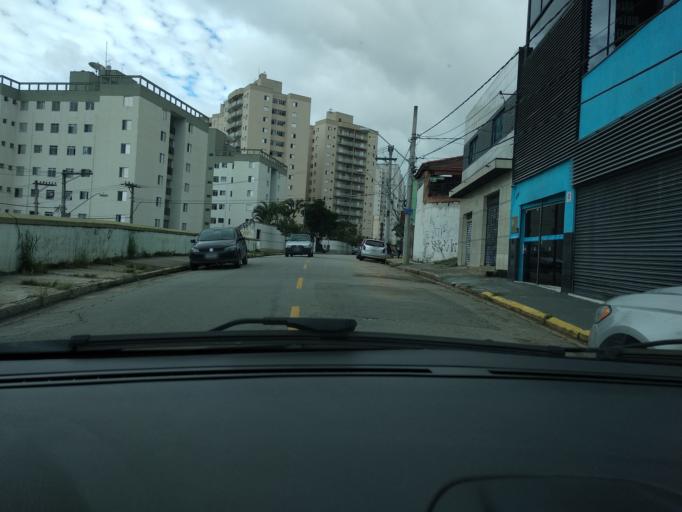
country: BR
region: Sao Paulo
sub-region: Mogi das Cruzes
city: Mogi das Cruzes
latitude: -23.5305
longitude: -46.1956
